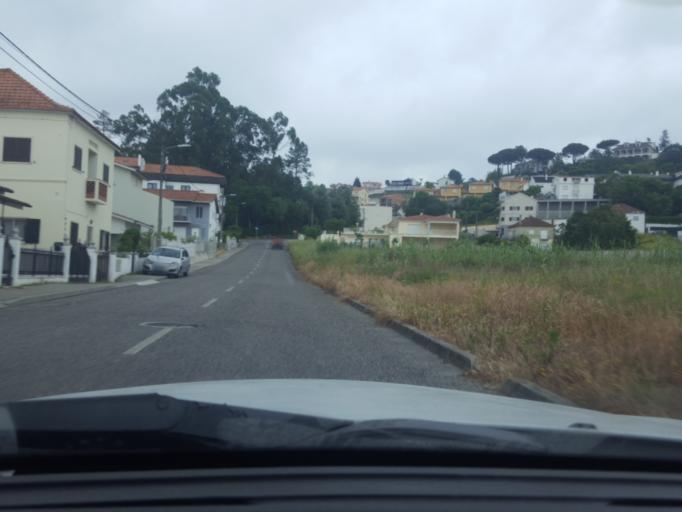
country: PT
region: Leiria
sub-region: Leiria
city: Leiria
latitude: 39.7317
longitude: -8.7929
